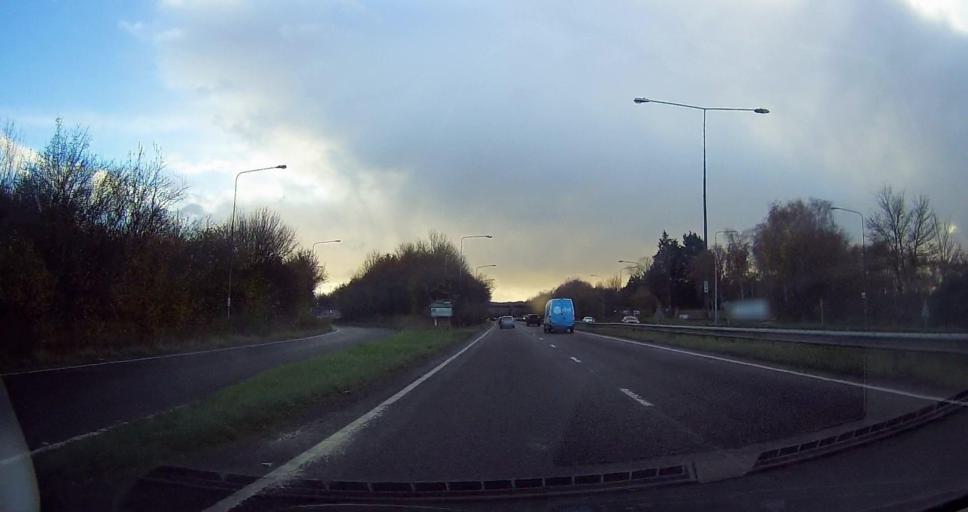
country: GB
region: England
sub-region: West Sussex
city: Hurstpierpoint
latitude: 50.9571
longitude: -0.1935
